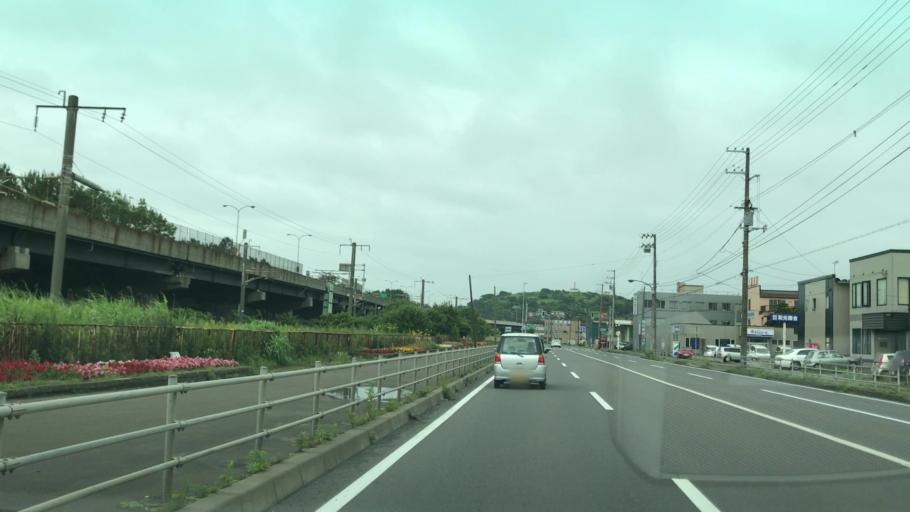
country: JP
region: Hokkaido
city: Muroran
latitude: 42.3355
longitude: 141.0104
